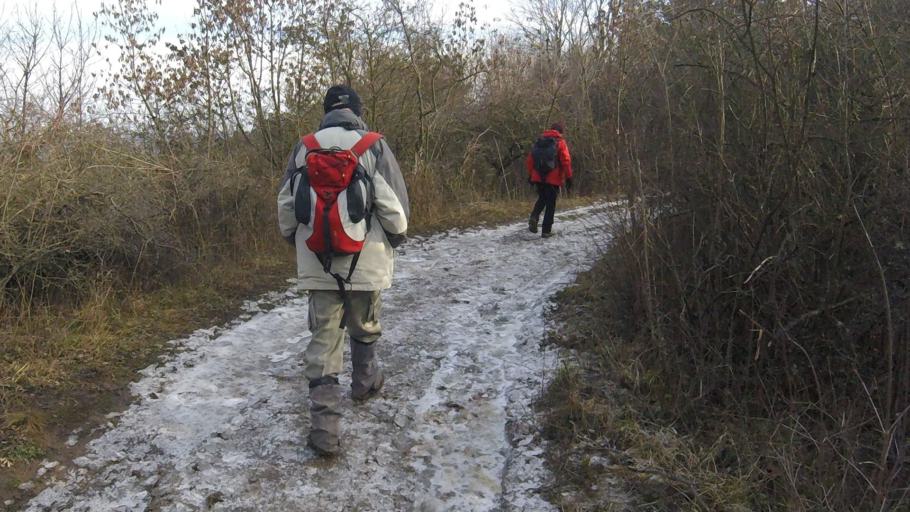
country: HU
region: Pest
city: Urom
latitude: 47.5965
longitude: 19.0332
